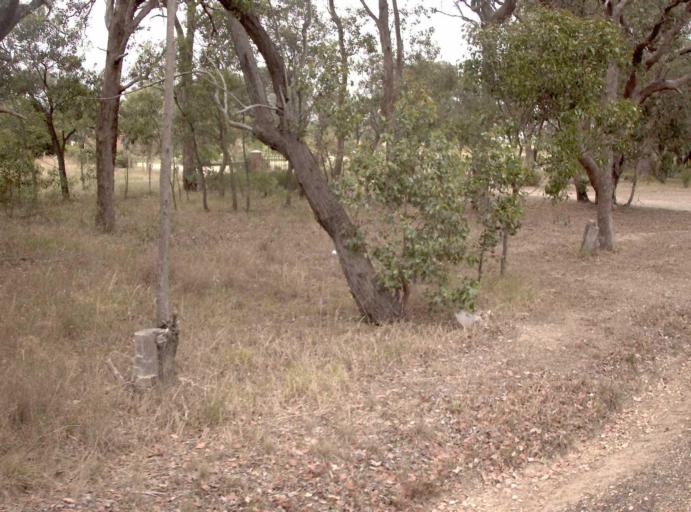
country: AU
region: Victoria
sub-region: Wellington
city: Heyfield
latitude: -37.9669
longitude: 146.7774
